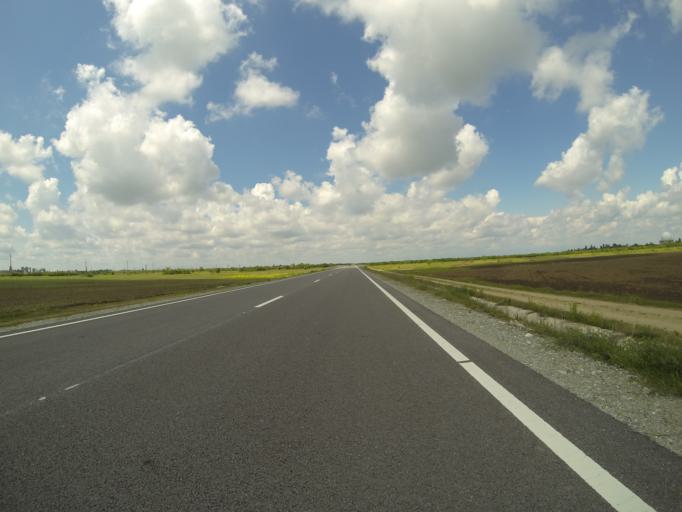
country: RO
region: Dolj
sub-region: Comuna Carcea
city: Carcea
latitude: 44.2746
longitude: 23.9104
